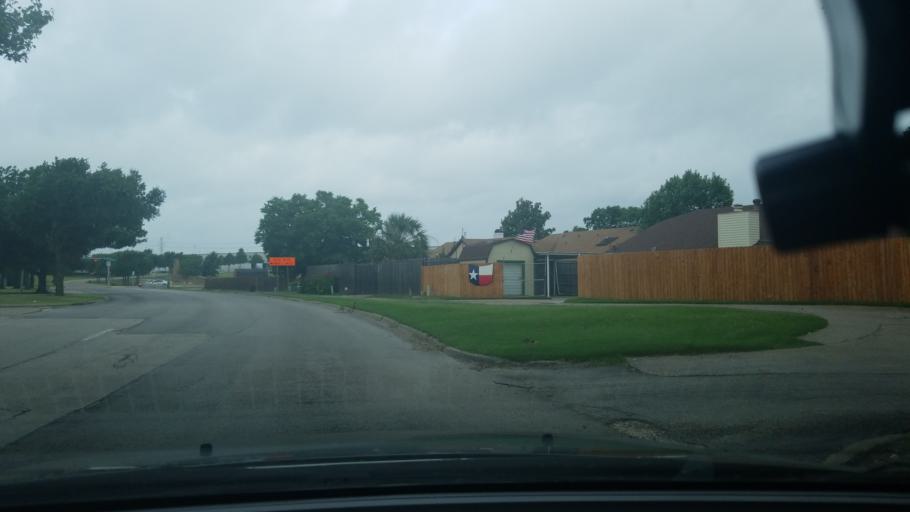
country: US
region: Texas
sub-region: Dallas County
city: Mesquite
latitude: 32.7816
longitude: -96.6443
